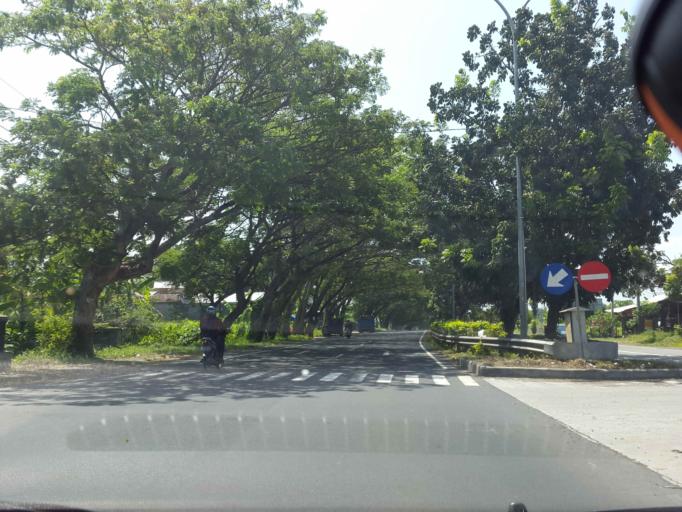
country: ID
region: Bali
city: Klungkung
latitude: -8.5682
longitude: 115.3746
